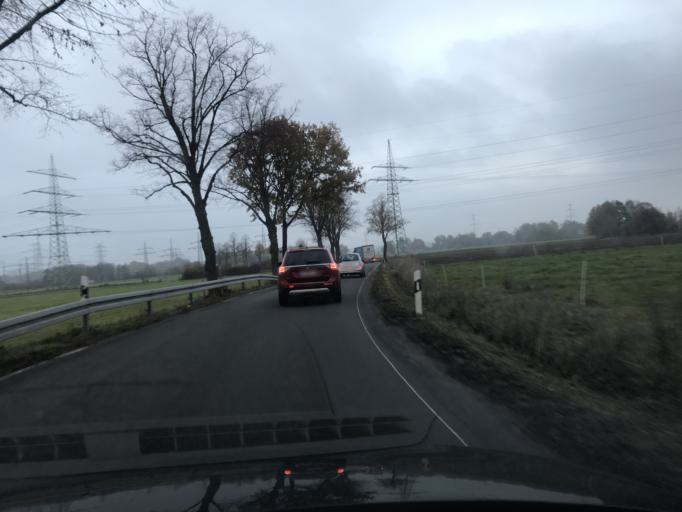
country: DE
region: North Rhine-Westphalia
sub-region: Regierungsbezirk Arnsberg
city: Welver
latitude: 51.6677
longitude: 7.9833
